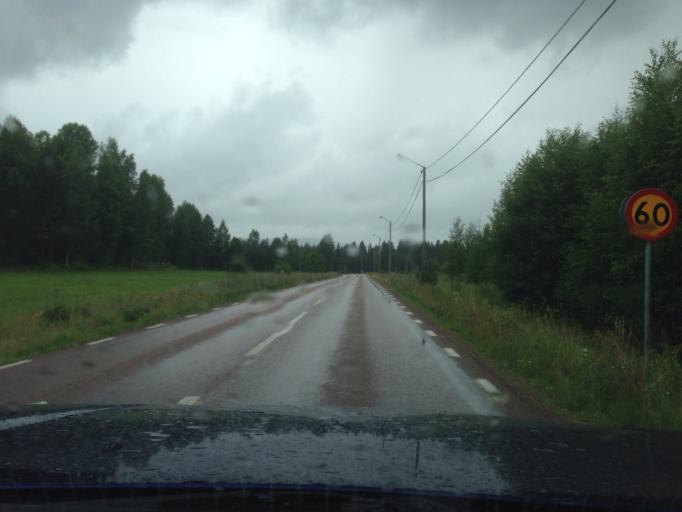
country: SE
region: Dalarna
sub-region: Ludvika Kommun
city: Grangesberg
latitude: 60.1465
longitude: 14.9862
